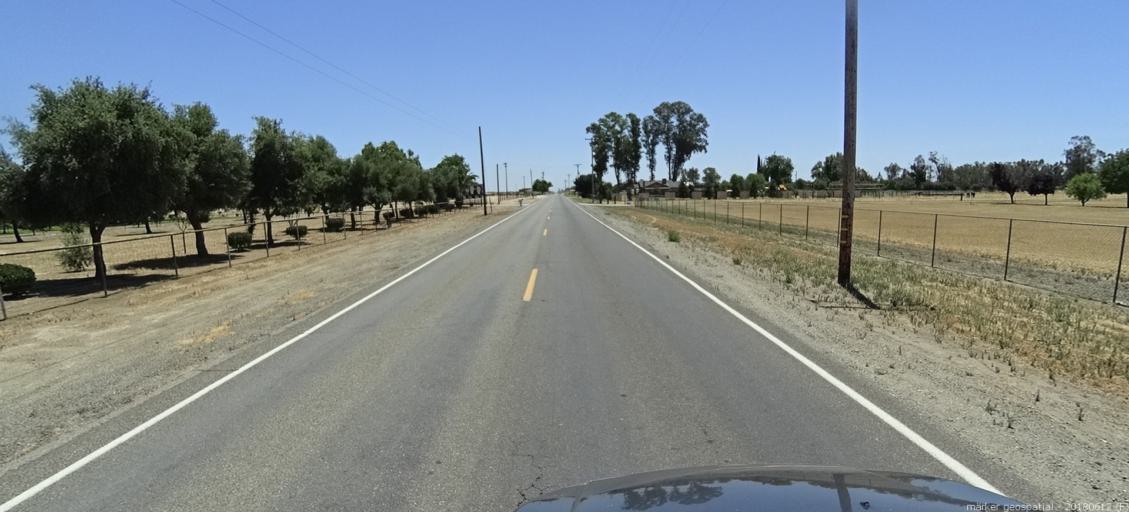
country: US
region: California
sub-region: Madera County
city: Chowchilla
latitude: 37.0901
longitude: -120.2568
